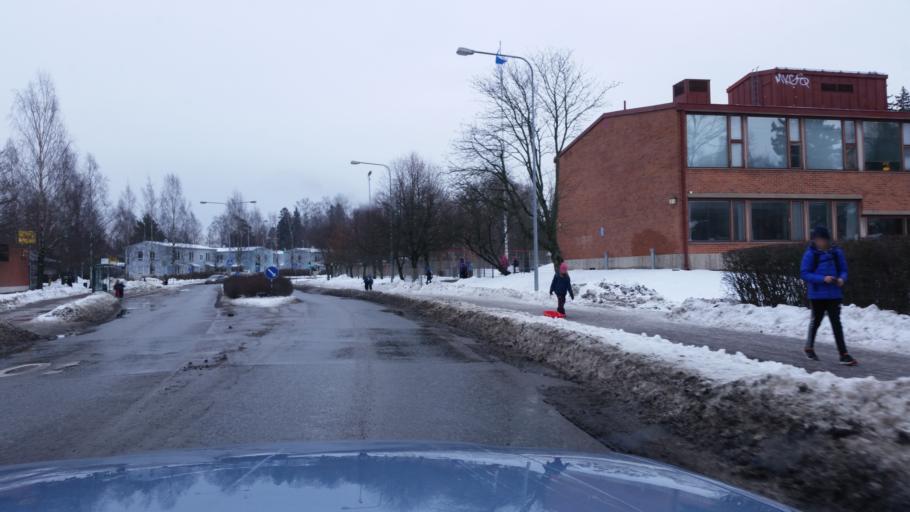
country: FI
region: Uusimaa
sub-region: Helsinki
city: Vantaa
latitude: 60.2711
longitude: 25.0501
